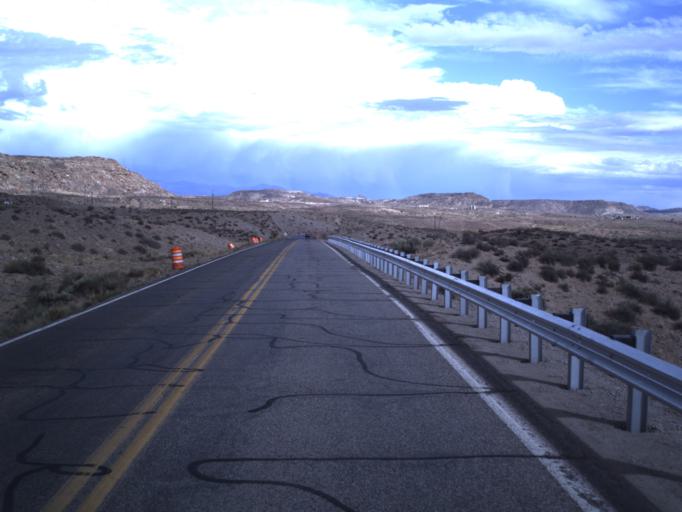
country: US
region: Utah
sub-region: San Juan County
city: Blanding
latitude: 37.2382
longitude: -109.2343
